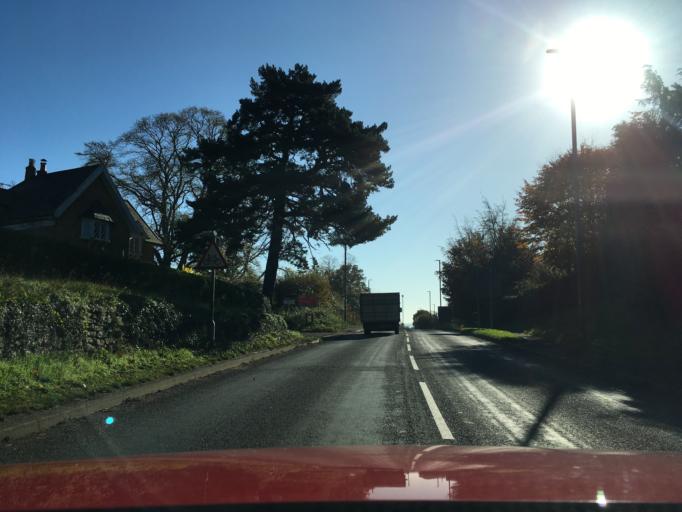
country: GB
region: England
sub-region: Somerset
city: Yeovil
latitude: 50.9305
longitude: -2.6407
